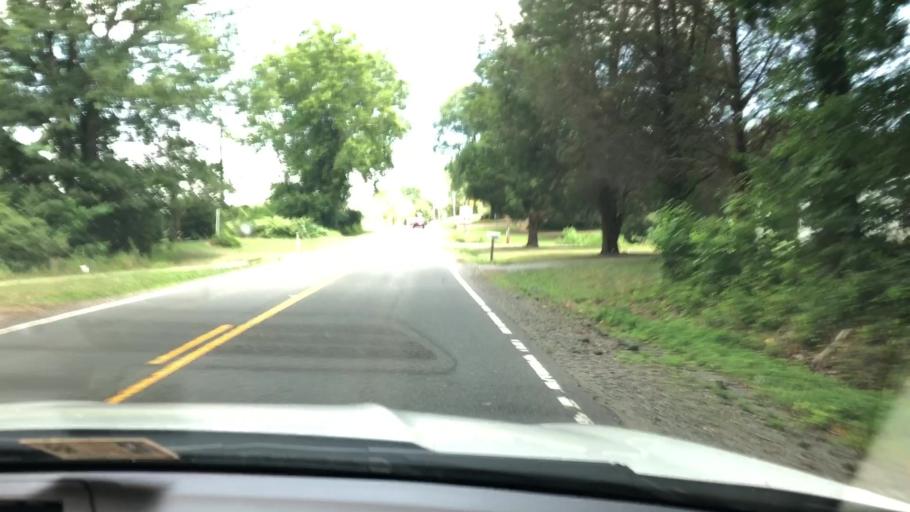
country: US
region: Virginia
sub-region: Lancaster County
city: Lancaster
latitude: 37.7699
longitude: -76.4690
